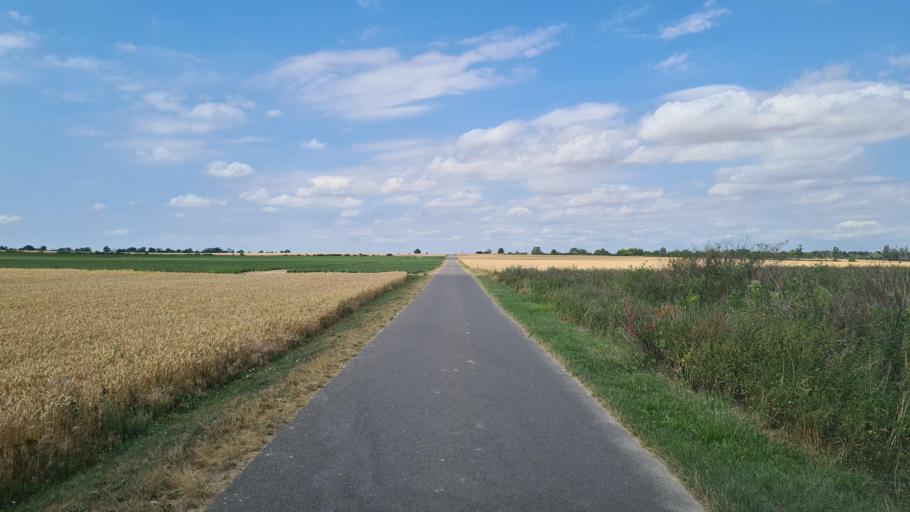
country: DE
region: Brandenburg
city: Juterbog
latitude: 51.9516
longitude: 13.0605
